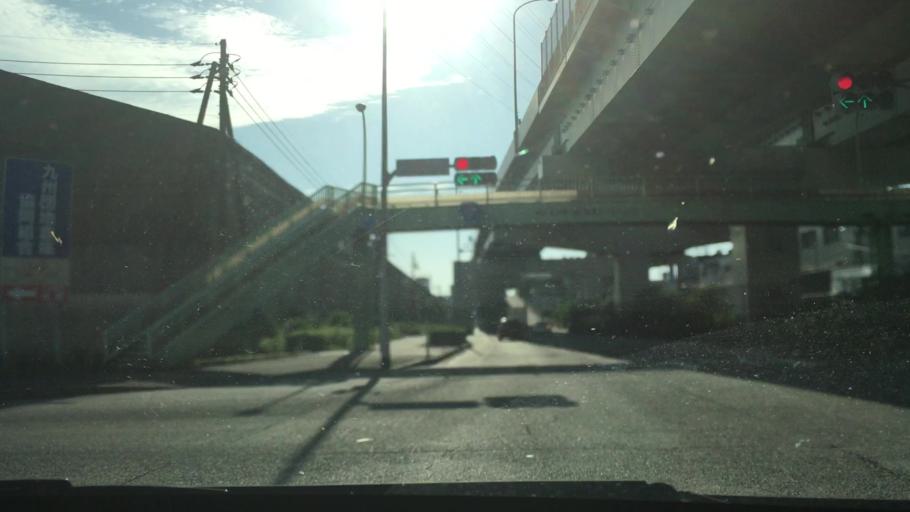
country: JP
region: Fukuoka
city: Fukuoka-shi
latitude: 33.6275
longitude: 130.4524
